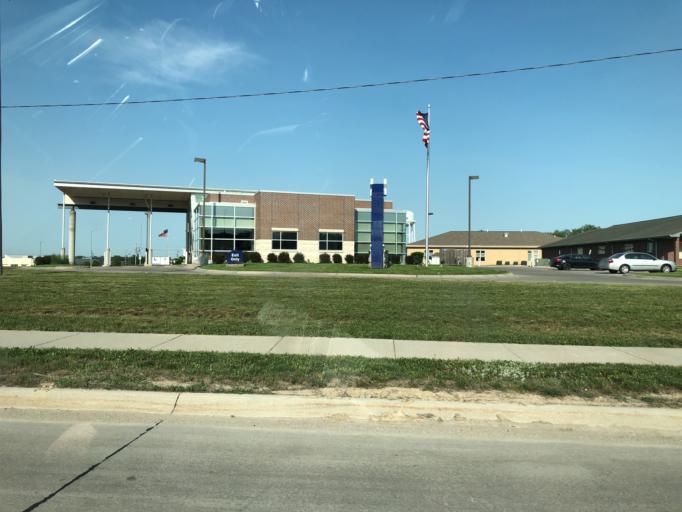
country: US
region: Nebraska
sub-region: Sarpy County
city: Gretna
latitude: 41.1462
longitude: -96.2389
